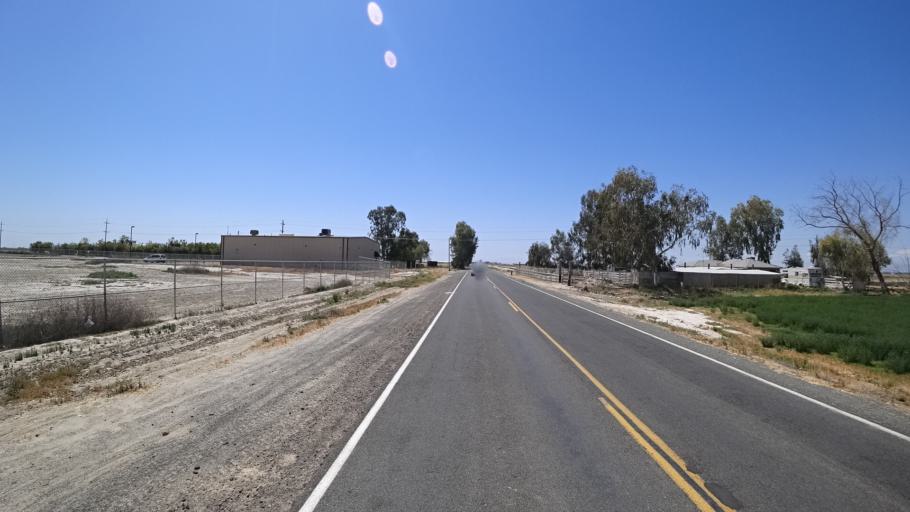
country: US
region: California
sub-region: Kings County
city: Stratford
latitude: 36.2265
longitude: -119.7625
